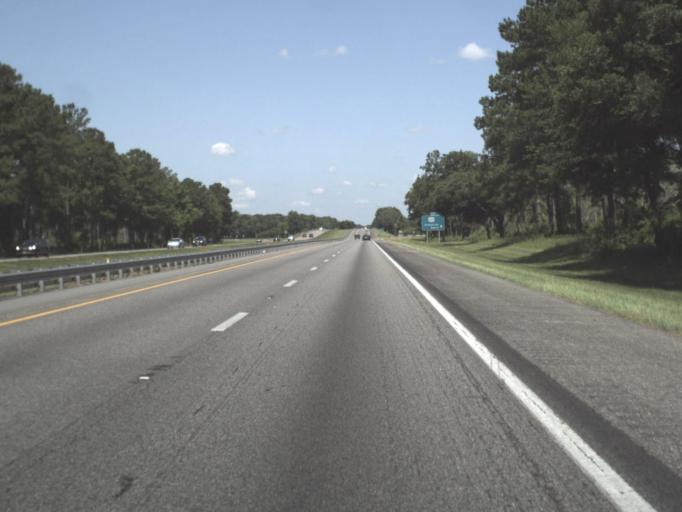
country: US
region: Florida
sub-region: Madison County
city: Madison
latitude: 30.4326
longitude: -83.6187
